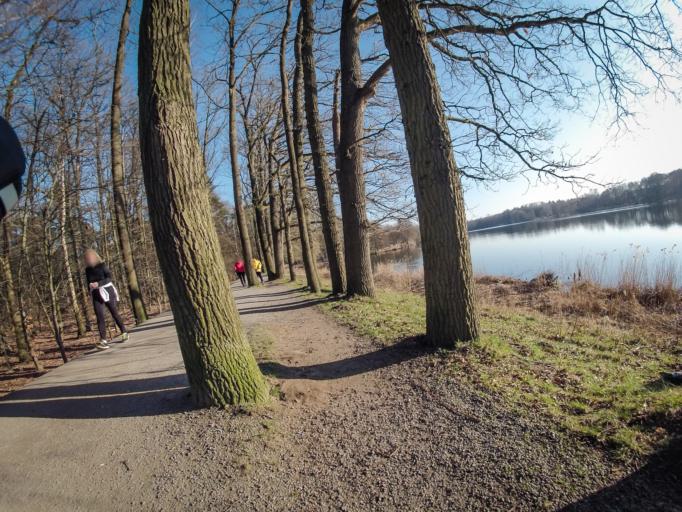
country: DE
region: Lower Saxony
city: Osnabrueck
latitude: 52.2878
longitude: 7.9903
